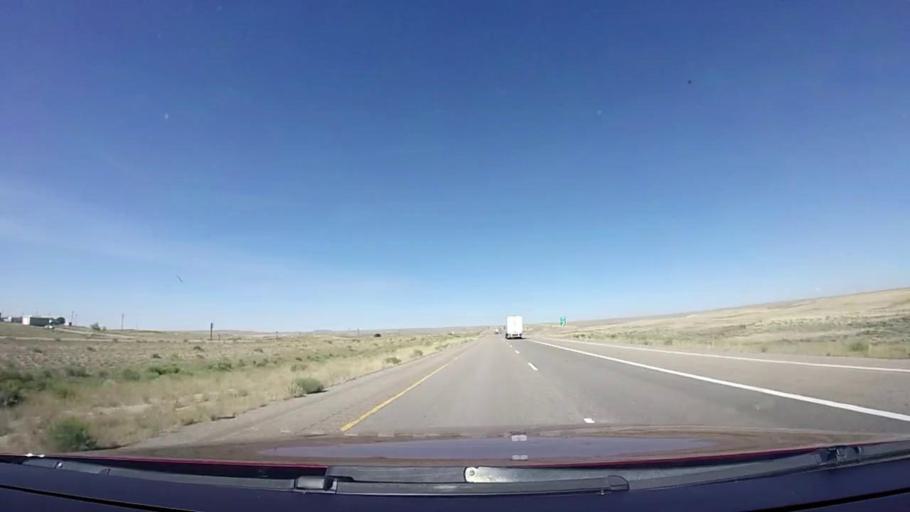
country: US
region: Wyoming
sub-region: Sweetwater County
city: Rock Springs
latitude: 41.6403
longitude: -108.4874
